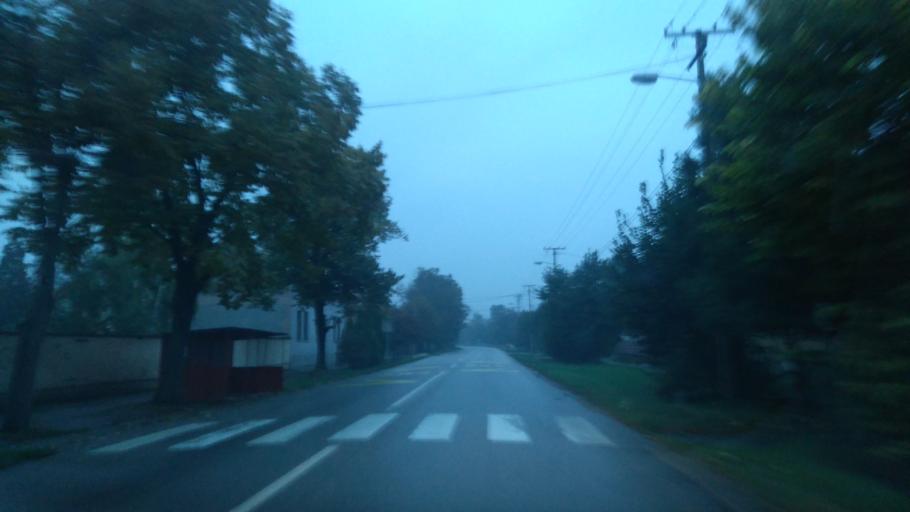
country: RS
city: Backo Petrovo Selo
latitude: 45.6965
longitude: 20.0833
